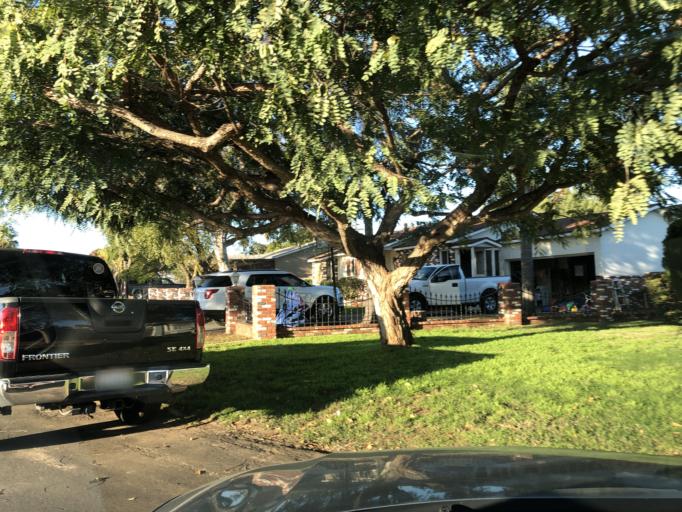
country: US
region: California
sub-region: San Diego County
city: Bonita
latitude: 32.6525
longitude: -117.0575
